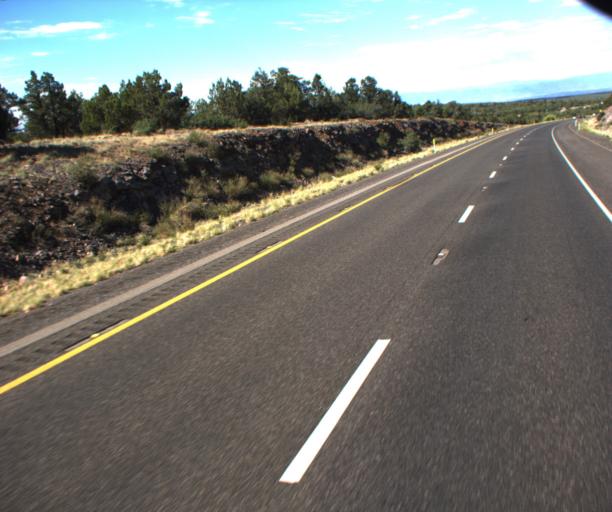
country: US
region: Arizona
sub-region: Yavapai County
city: Village of Oak Creek (Big Park)
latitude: 34.7857
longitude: -111.6081
